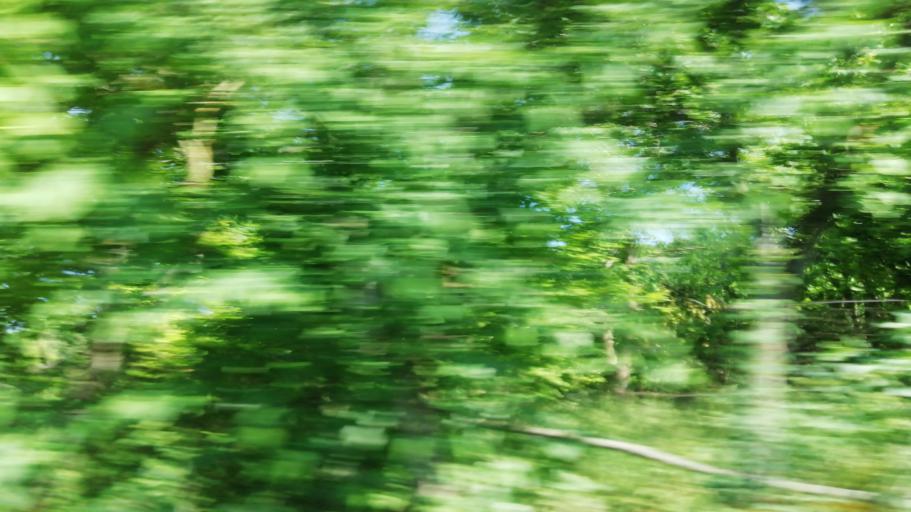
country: TR
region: Karabuk
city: Karabuk
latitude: 41.0860
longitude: 32.5817
